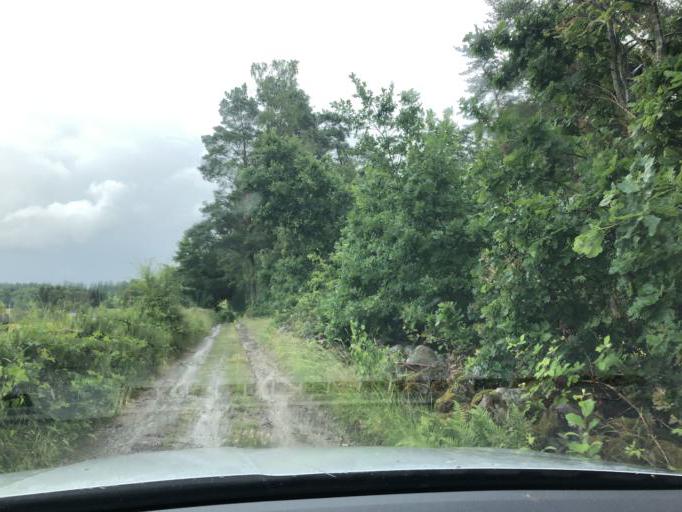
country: SE
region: Blekinge
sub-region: Solvesborgs Kommun
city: Soelvesborg
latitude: 56.1306
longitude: 14.6035
